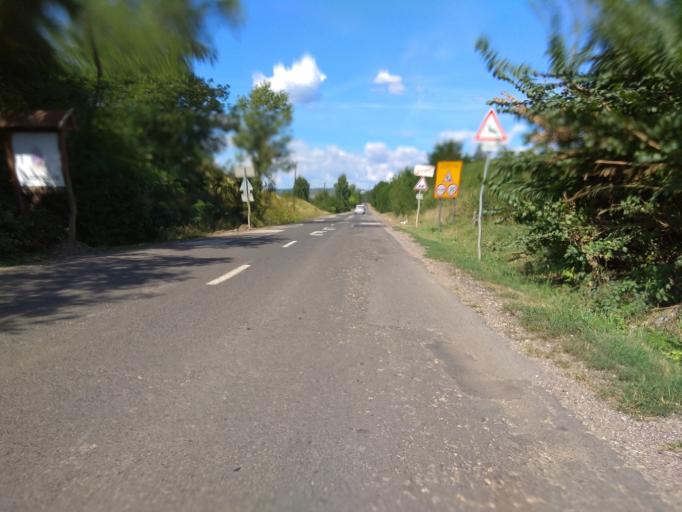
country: HU
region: Borsod-Abauj-Zemplen
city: Izsofalva
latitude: 48.2797
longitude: 20.6434
